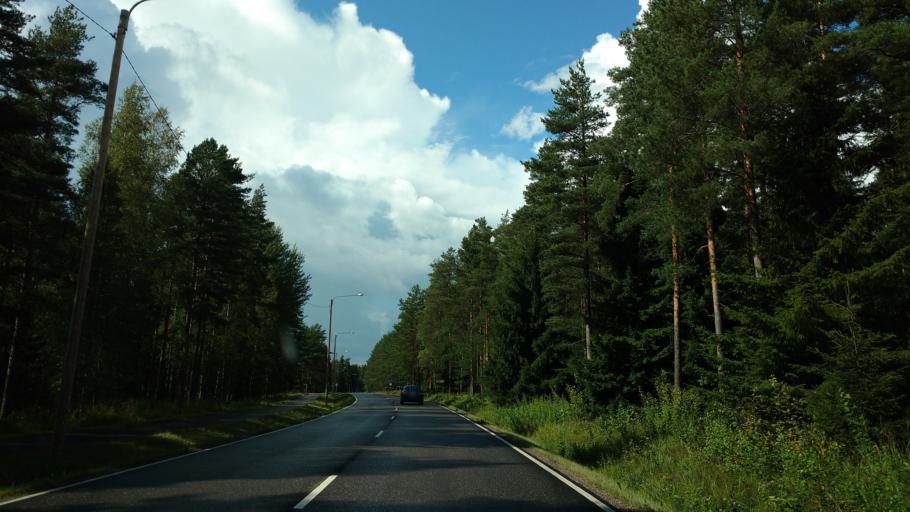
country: FI
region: Varsinais-Suomi
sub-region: Turku
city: Paimio
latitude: 60.4345
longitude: 22.7170
